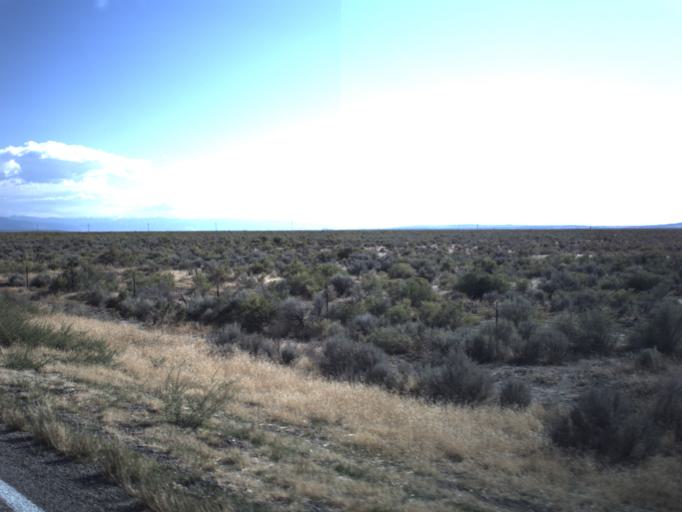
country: US
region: Utah
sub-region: Millard County
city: Delta
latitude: 39.2495
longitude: -112.4388
